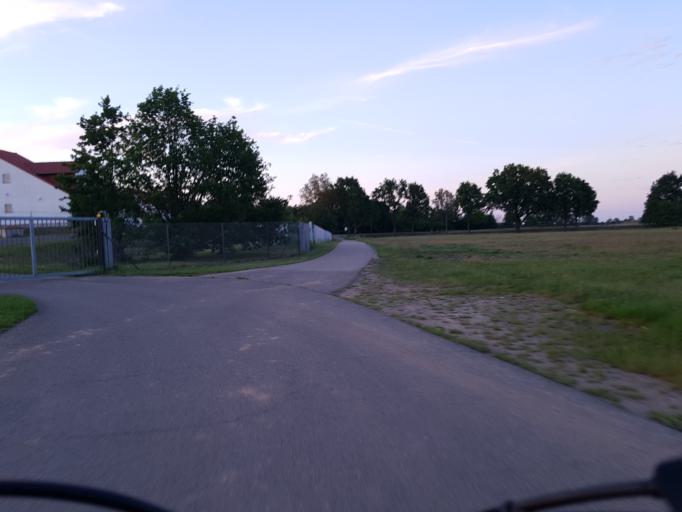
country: DE
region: Brandenburg
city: Falkenberg
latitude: 51.6081
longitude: 13.3046
